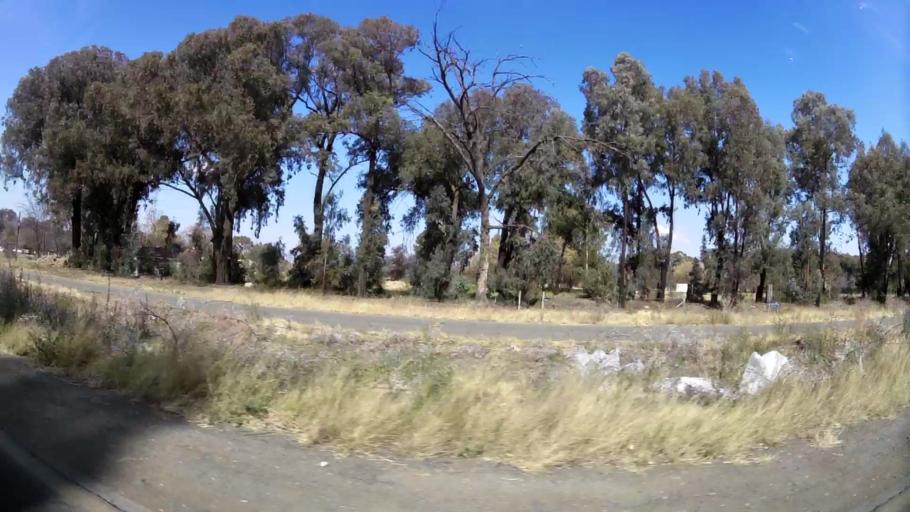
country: ZA
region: Orange Free State
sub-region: Mangaung Metropolitan Municipality
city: Bloemfontein
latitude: -29.1160
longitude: 26.2557
